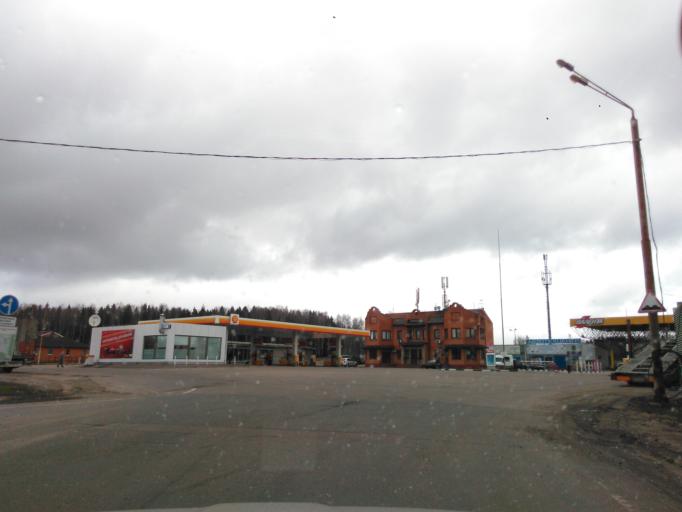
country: RU
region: Moskovskaya
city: Rzhavki
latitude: 56.0034
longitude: 37.2360
